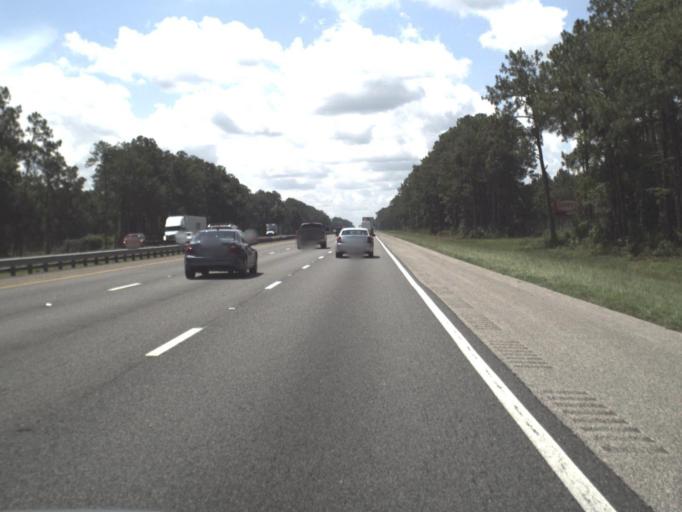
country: US
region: Florida
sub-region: Saint Johns County
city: Saint Augustine Shores
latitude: 29.7917
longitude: -81.3643
